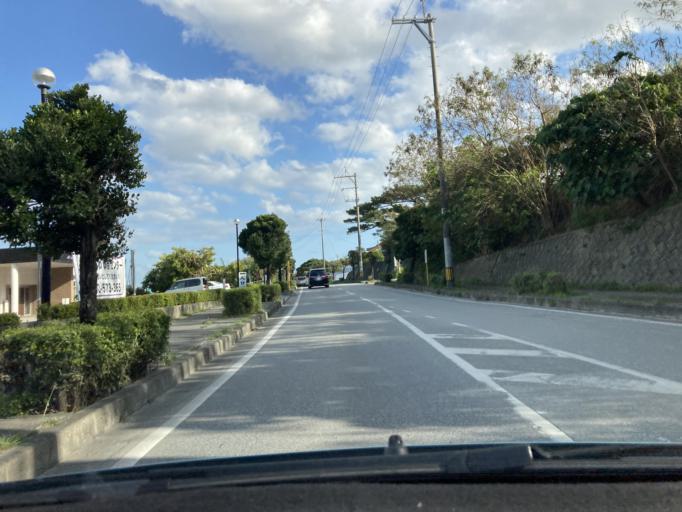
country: JP
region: Okinawa
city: Tomigusuku
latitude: 26.1908
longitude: 127.7034
